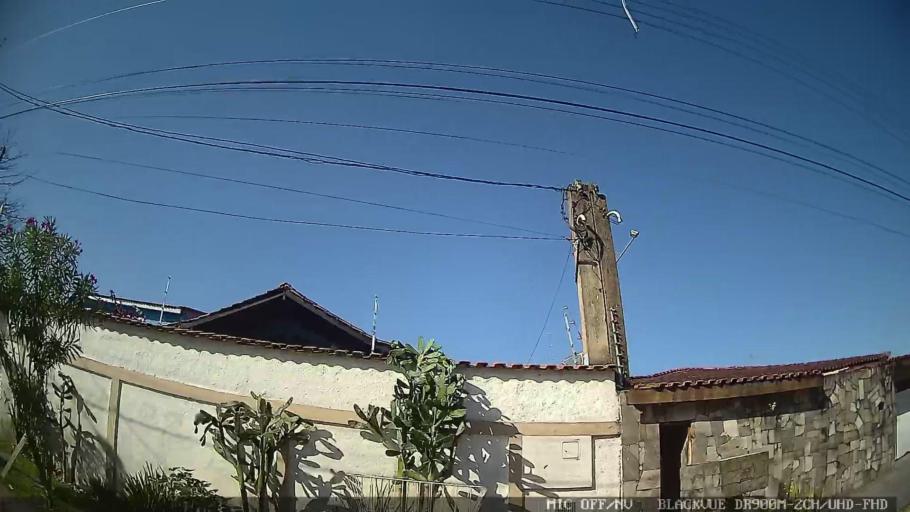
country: BR
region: Sao Paulo
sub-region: Guaruja
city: Guaruja
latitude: -23.9739
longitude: -46.2111
